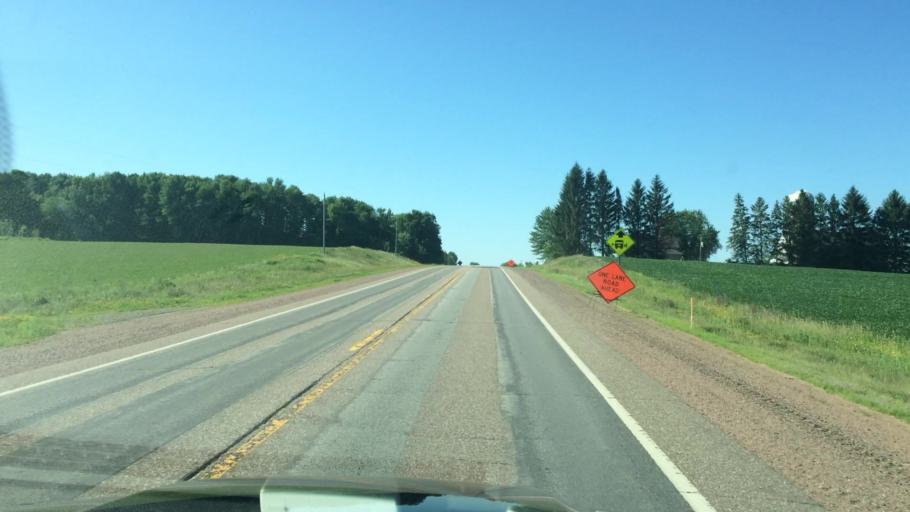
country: US
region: Wisconsin
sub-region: Marathon County
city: Stratford
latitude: 44.9116
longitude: -90.0786
